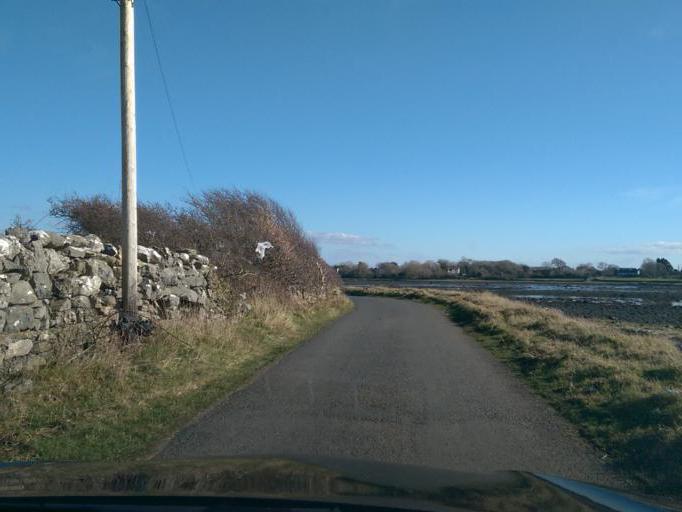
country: IE
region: Connaught
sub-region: County Galway
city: Oranmore
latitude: 53.2388
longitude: -8.9556
